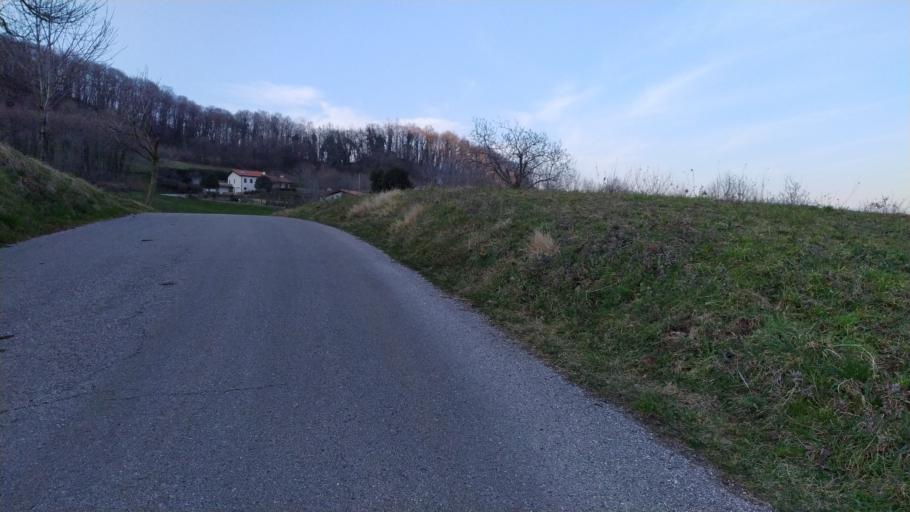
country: IT
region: Veneto
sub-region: Provincia di Vicenza
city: Monte di Malo
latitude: 45.6629
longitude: 11.3493
